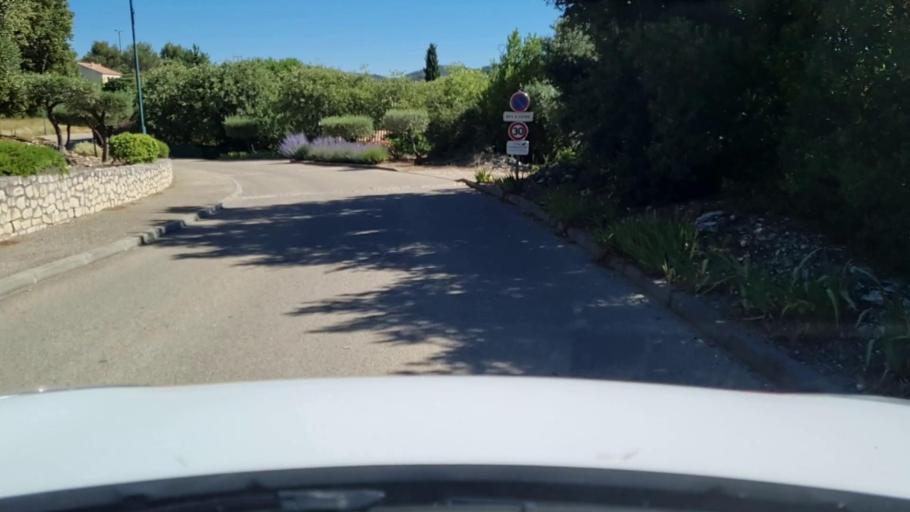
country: FR
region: Languedoc-Roussillon
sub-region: Departement du Gard
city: Villevieille
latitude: 43.8494
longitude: 4.1083
